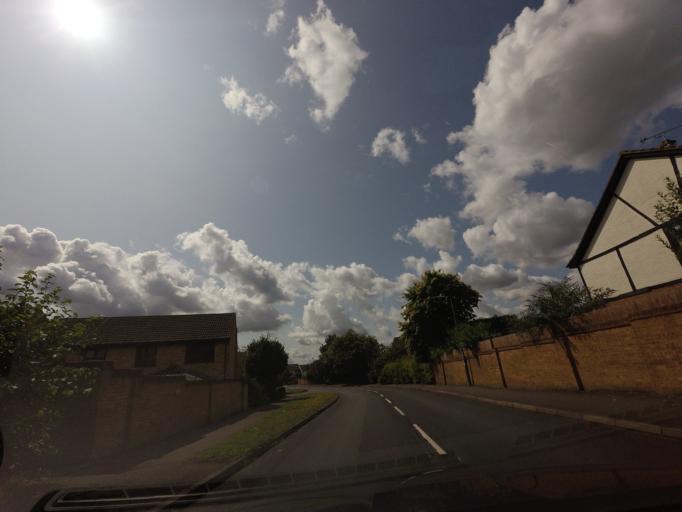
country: GB
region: England
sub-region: Kent
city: Boxley
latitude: 51.2781
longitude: 0.5525
